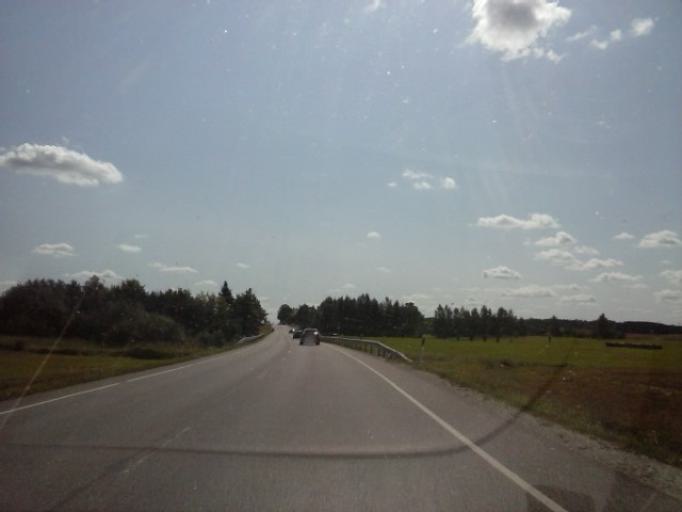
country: EE
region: Tartu
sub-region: UElenurme vald
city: Ulenurme
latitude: 58.2436
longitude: 26.7848
